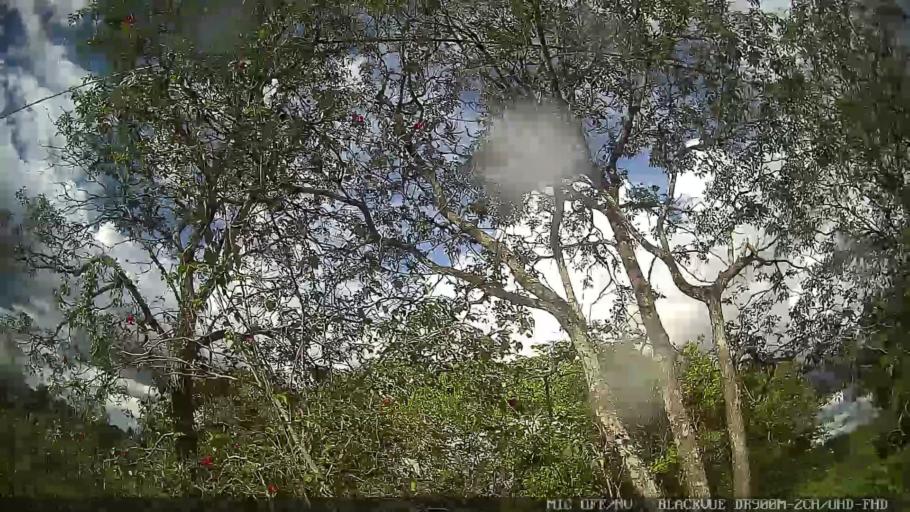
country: BR
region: Sao Paulo
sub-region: Jaguariuna
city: Jaguariuna
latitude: -22.6612
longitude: -47.0403
